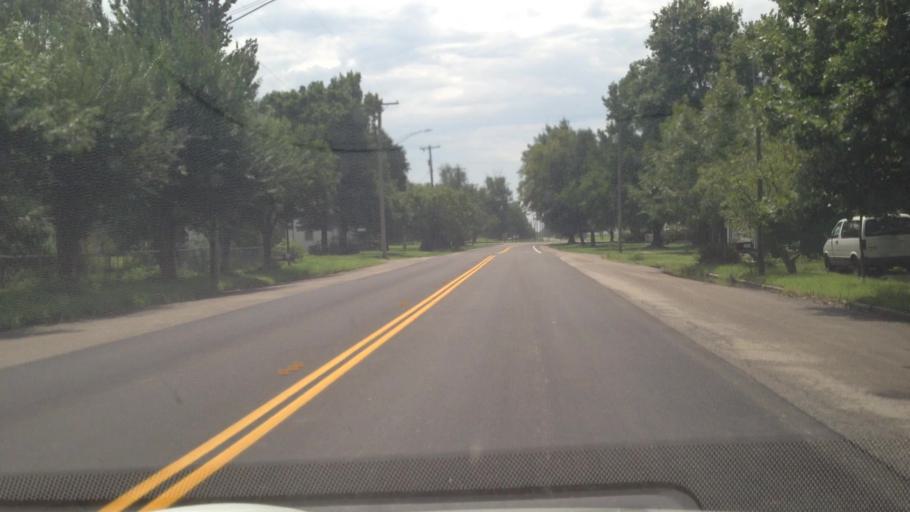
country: US
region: Kansas
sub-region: Crawford County
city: Girard
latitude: 37.6618
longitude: -94.9696
